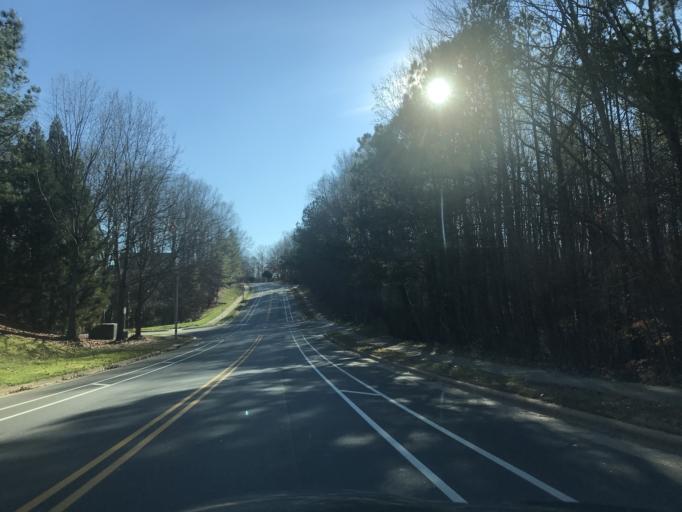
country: US
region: North Carolina
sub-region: Wake County
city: Cary
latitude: 35.7983
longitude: -78.7384
